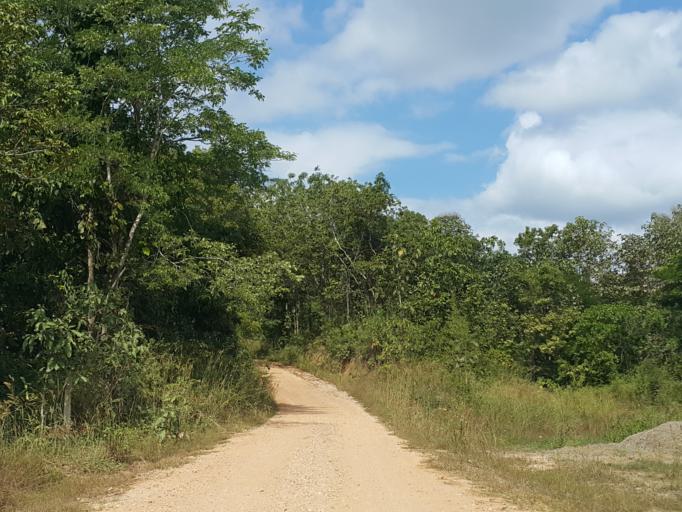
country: TH
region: Lampang
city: Hang Chat
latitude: 18.4811
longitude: 99.4160
